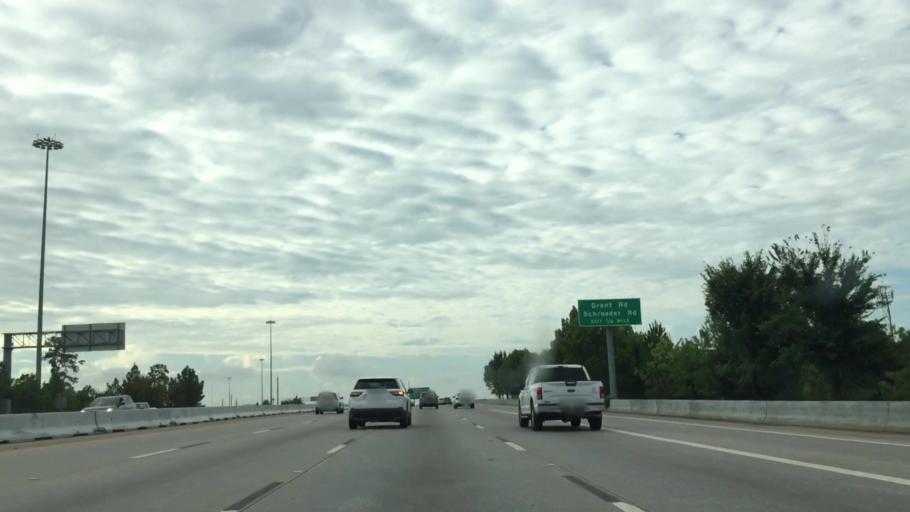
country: US
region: Texas
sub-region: Harris County
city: Oak Cliff Place
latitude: 29.9753
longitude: -95.5648
